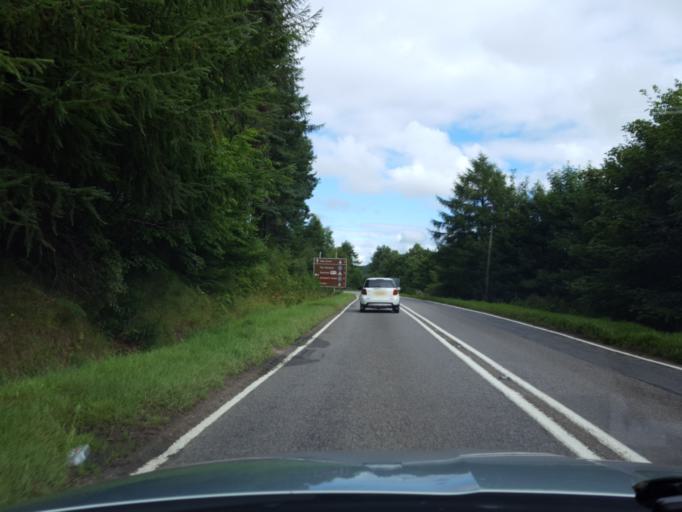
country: GB
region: Scotland
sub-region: Moray
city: Rothes
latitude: 57.4960
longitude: -3.1902
